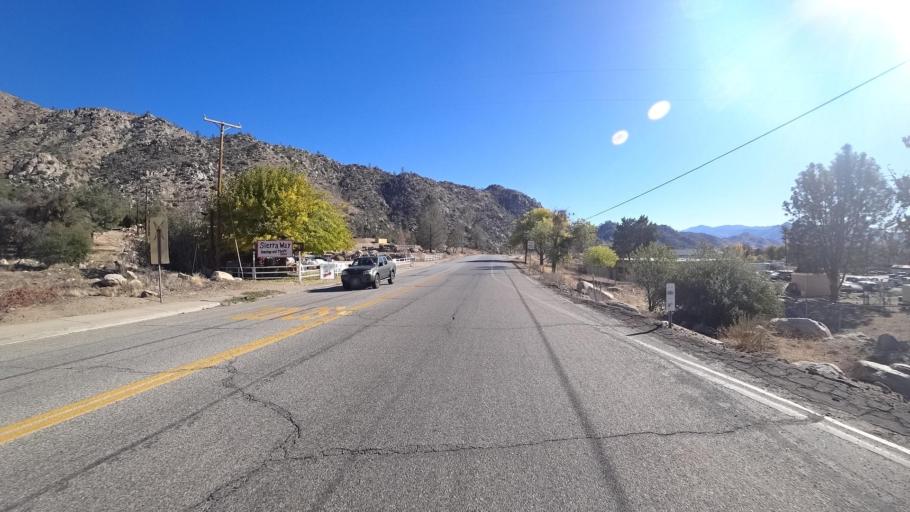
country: US
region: California
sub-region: Kern County
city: Kernville
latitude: 35.7554
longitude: -118.4176
